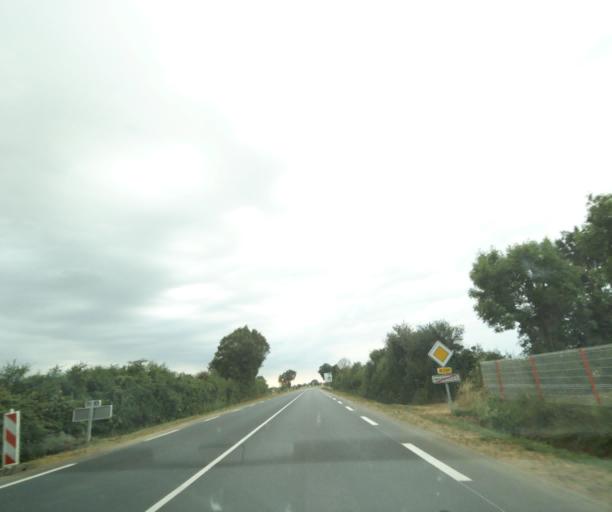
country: FR
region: Pays de la Loire
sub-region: Departement de la Vendee
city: Champagne-les-Marais
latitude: 46.4244
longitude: -1.0884
